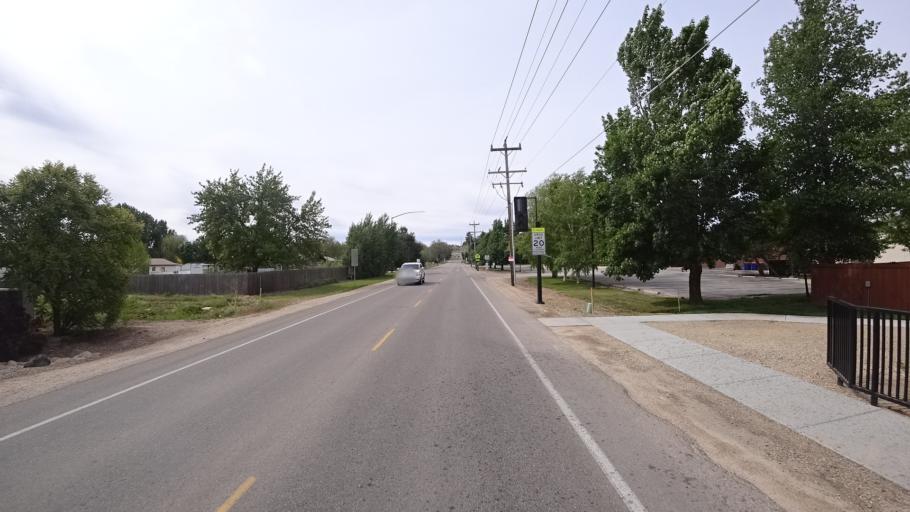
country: US
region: Idaho
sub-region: Ada County
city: Meridian
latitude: 43.5393
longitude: -116.3145
